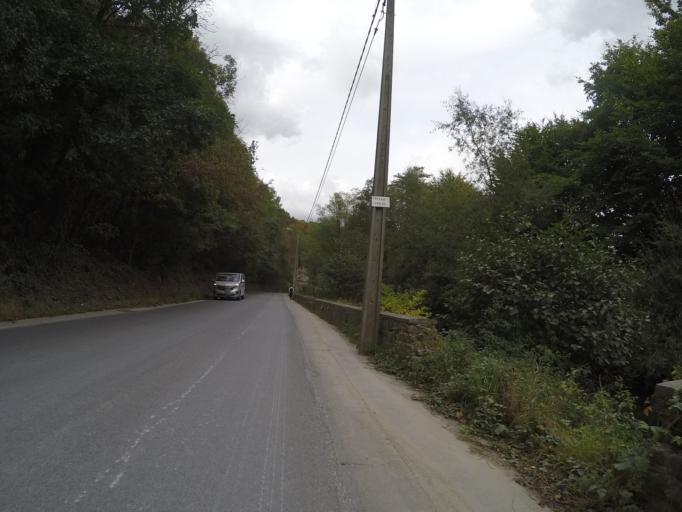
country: BE
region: Wallonia
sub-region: Province de Namur
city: Yvoir
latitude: 50.3303
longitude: 4.8969
